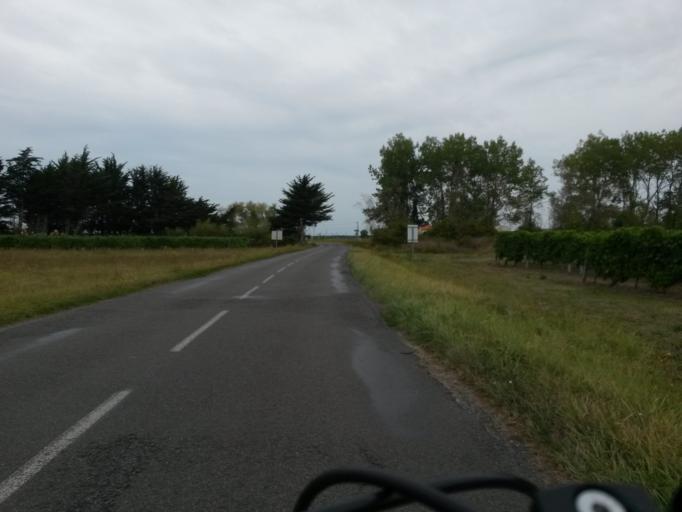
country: FR
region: Poitou-Charentes
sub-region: Departement de la Charente-Maritime
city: Dolus-d'Oleron
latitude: 45.9321
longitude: -1.3326
